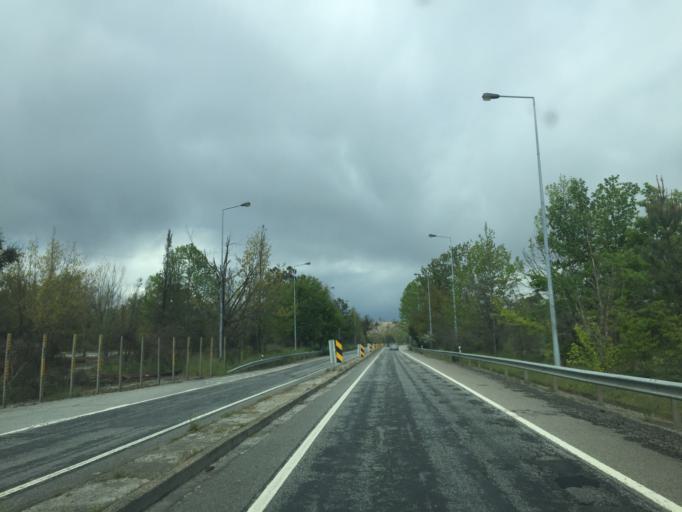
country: PT
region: Viseu
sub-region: Vouzela
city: Vouzela
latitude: 40.6507
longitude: -8.0412
